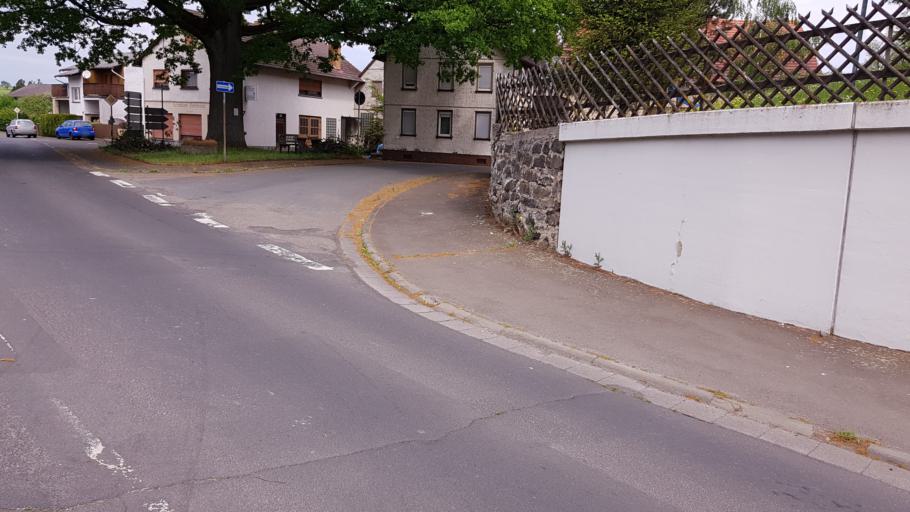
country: DE
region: Hesse
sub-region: Regierungsbezirk Giessen
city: Grunberg
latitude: 50.6485
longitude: 9.0261
